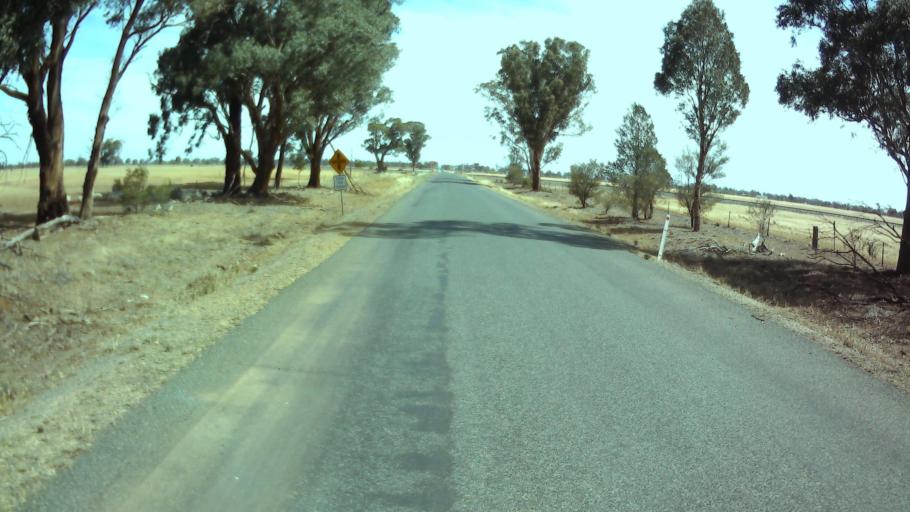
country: AU
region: New South Wales
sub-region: Weddin
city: Grenfell
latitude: -33.9818
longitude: 147.7778
